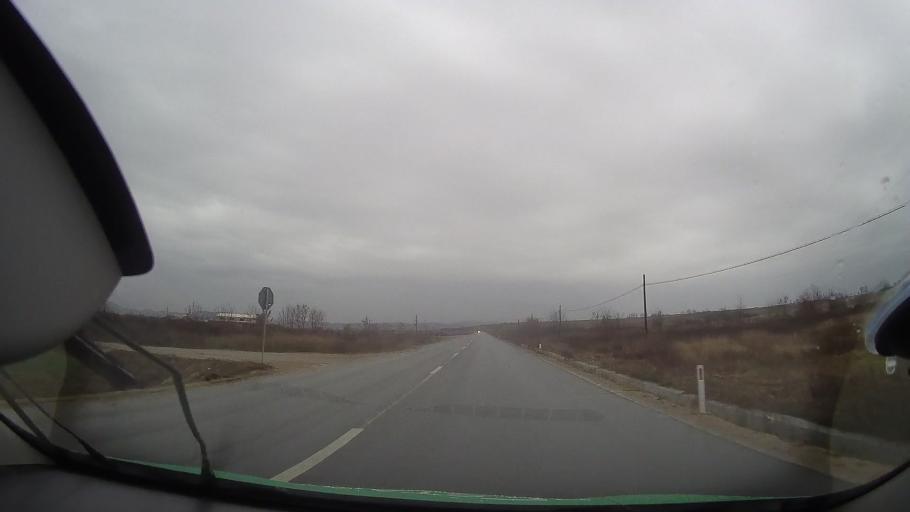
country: RO
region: Bihor
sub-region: Municipiul Beius
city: Beius
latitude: 46.6762
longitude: 22.3219
